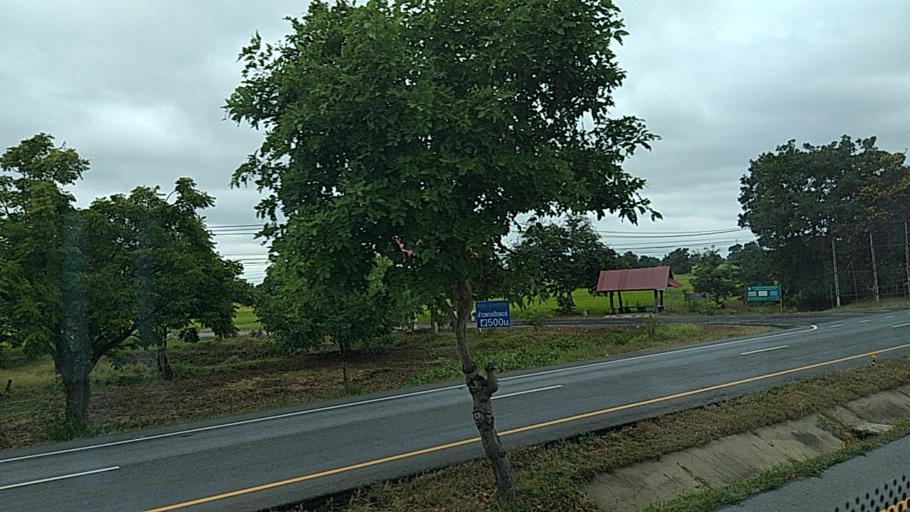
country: TH
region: Nakhon Ratchasima
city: Bua Lai
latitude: 15.7139
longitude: 102.5892
